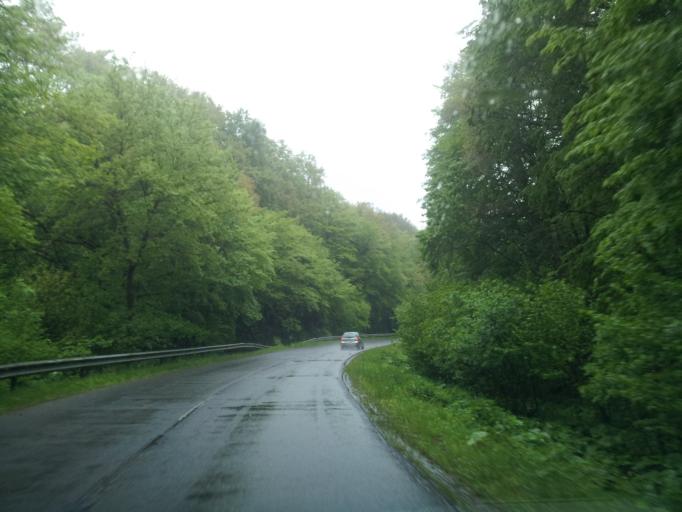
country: HU
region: Baranya
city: Komlo
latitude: 46.2034
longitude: 18.3000
